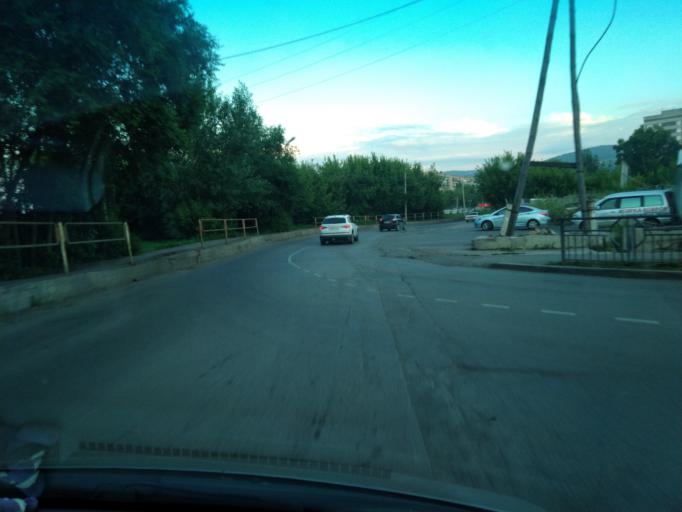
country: RU
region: Krasnoyarskiy
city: Krasnoyarsk
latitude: 55.9857
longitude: 92.8707
